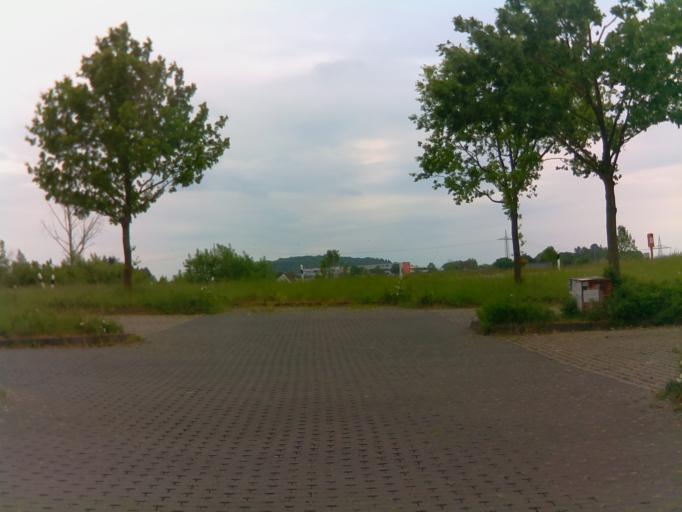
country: DE
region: Hesse
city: Staufenberg
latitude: 50.6659
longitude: 8.7218
